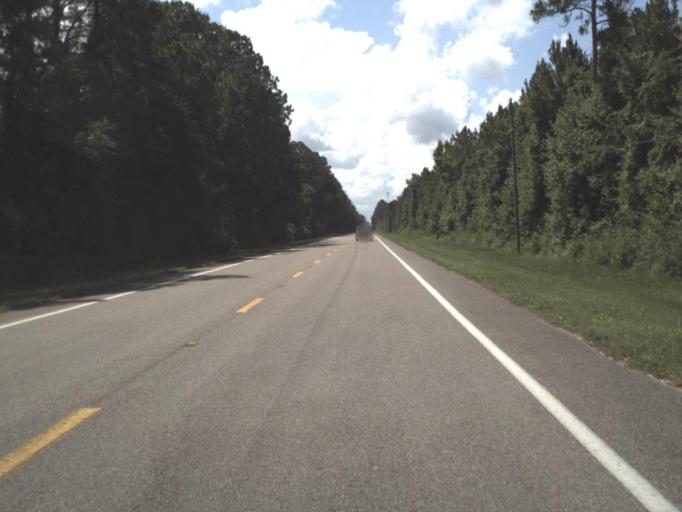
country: US
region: Florida
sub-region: Putnam County
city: East Palatka
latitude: 29.5527
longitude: -81.5340
